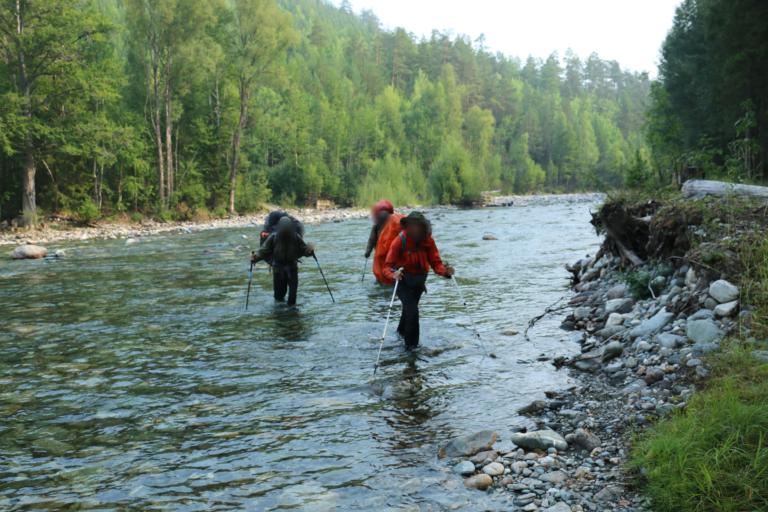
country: RU
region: Respublika Buryatiya
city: Nizhneangarsk
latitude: 56.0768
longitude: 109.7364
